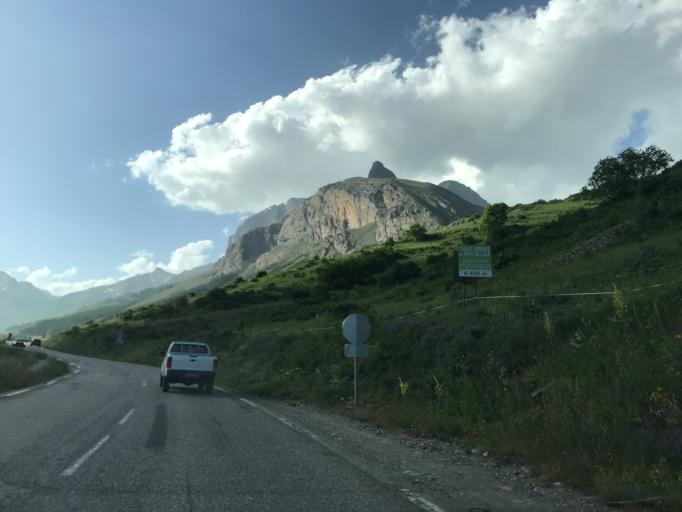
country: FR
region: Provence-Alpes-Cote d'Azur
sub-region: Departement des Hautes-Alpes
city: Le Monetier-les-Bains
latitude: 45.0143
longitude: 6.4673
